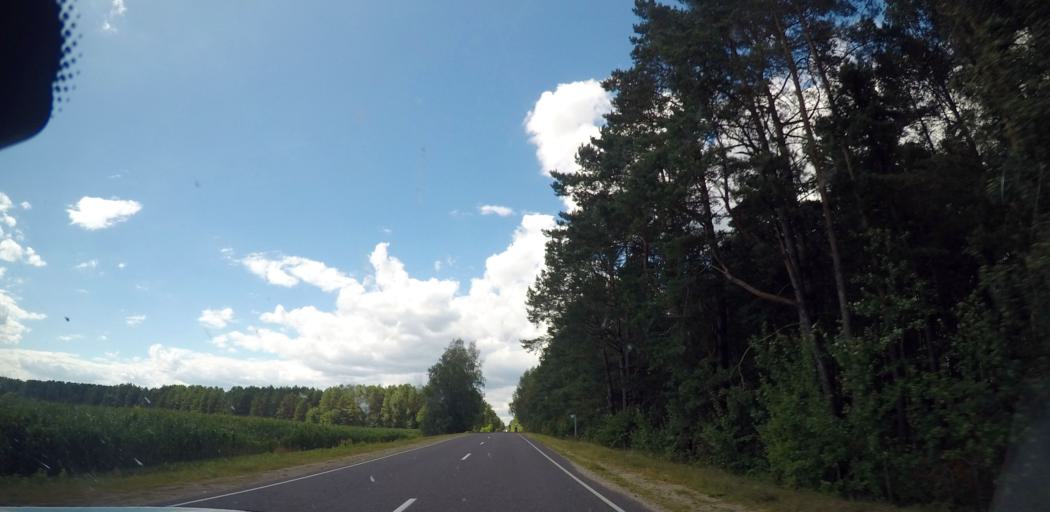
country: LT
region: Alytaus apskritis
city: Druskininkai
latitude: 53.8731
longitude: 24.1549
